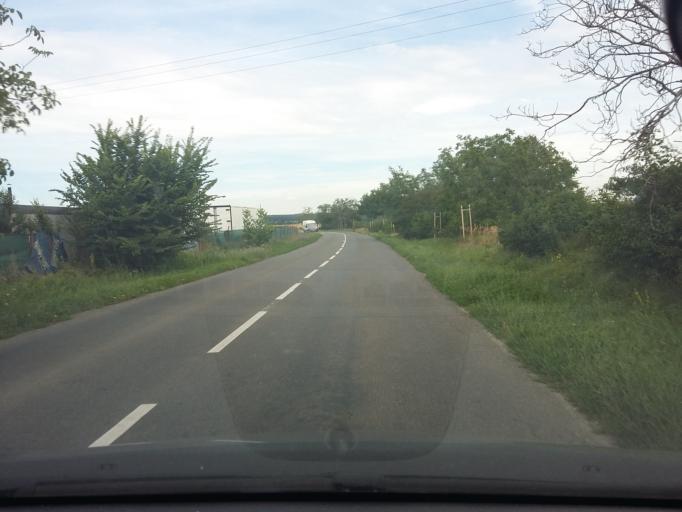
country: SK
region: Bratislavsky
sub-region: Okres Pezinok
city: Pezinok
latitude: 48.2580
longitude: 17.2865
